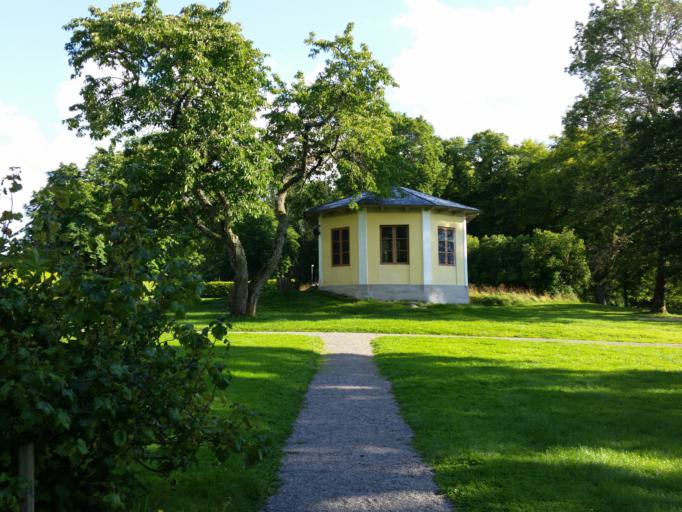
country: SE
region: Soedermanland
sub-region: Strangnas Kommun
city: Mariefred
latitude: 59.2459
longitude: 17.3086
